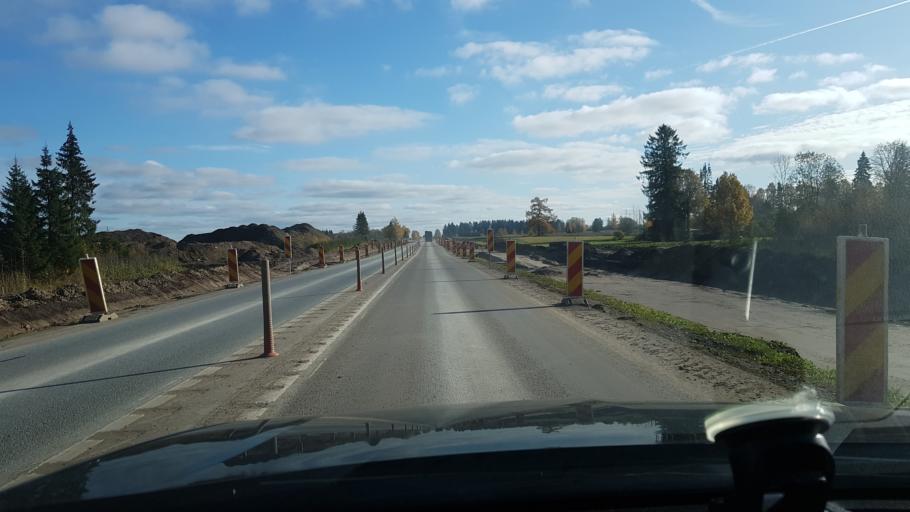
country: EE
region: Laeaene-Virumaa
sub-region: Kadrina vald
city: Kadrina
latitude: 59.4373
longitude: 26.1496
